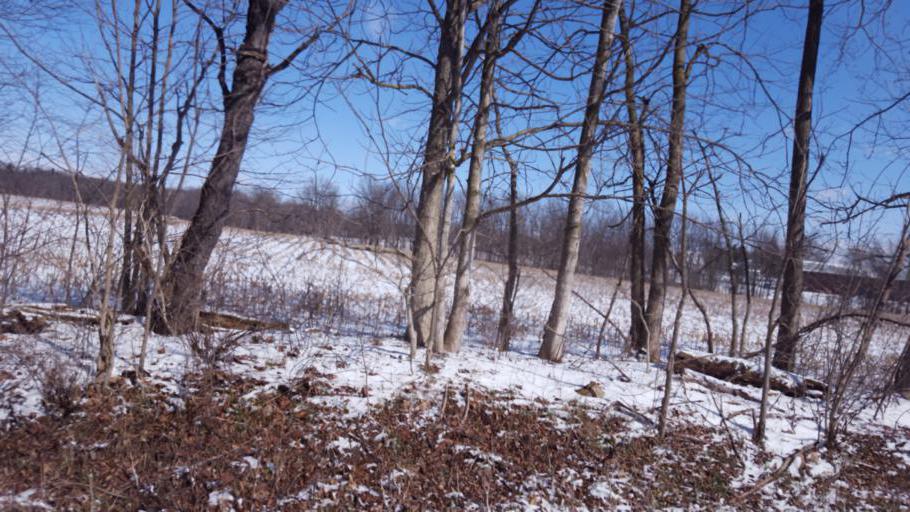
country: US
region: Ohio
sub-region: Morrow County
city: Mount Gilead
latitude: 40.4810
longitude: -82.6937
